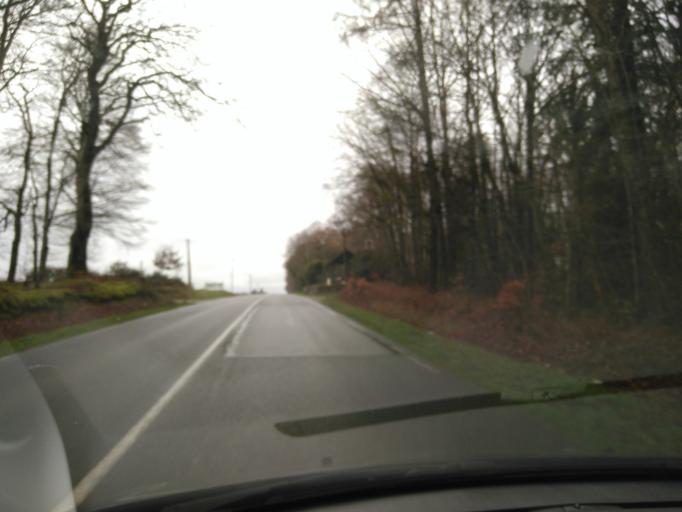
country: FR
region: Limousin
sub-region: Departement de la Haute-Vienne
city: Solignac
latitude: 45.7238
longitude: 1.2566
